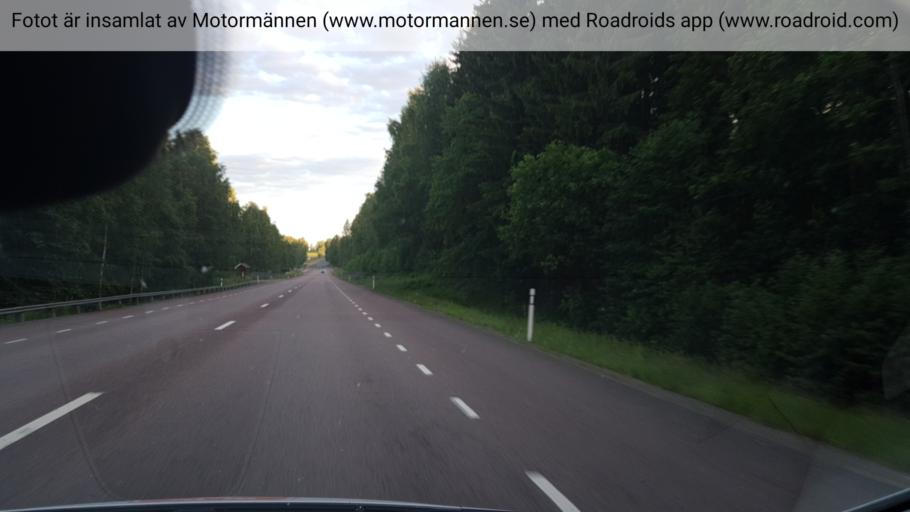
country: SE
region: Vaermland
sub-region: Sunne Kommun
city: Sunne
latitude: 59.8236
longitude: 13.1322
